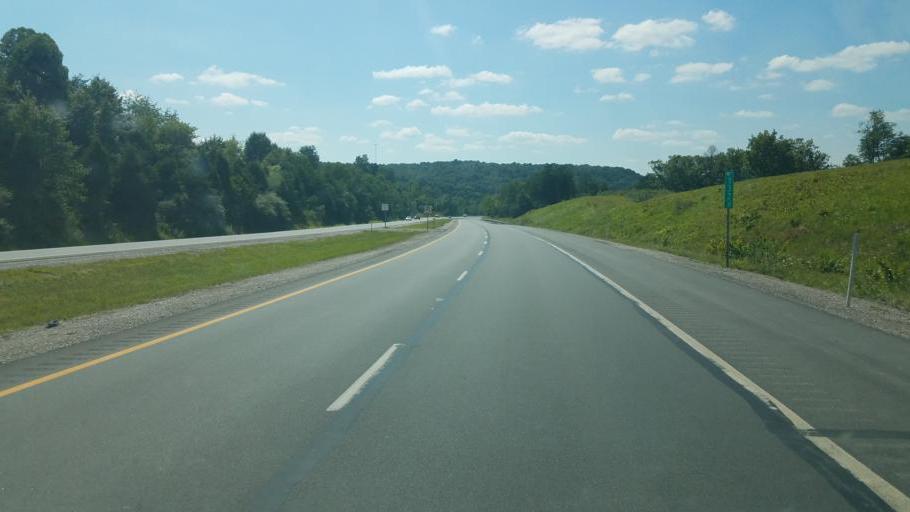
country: US
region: West Virginia
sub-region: Jackson County
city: Ripley
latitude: 38.7613
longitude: -81.6986
